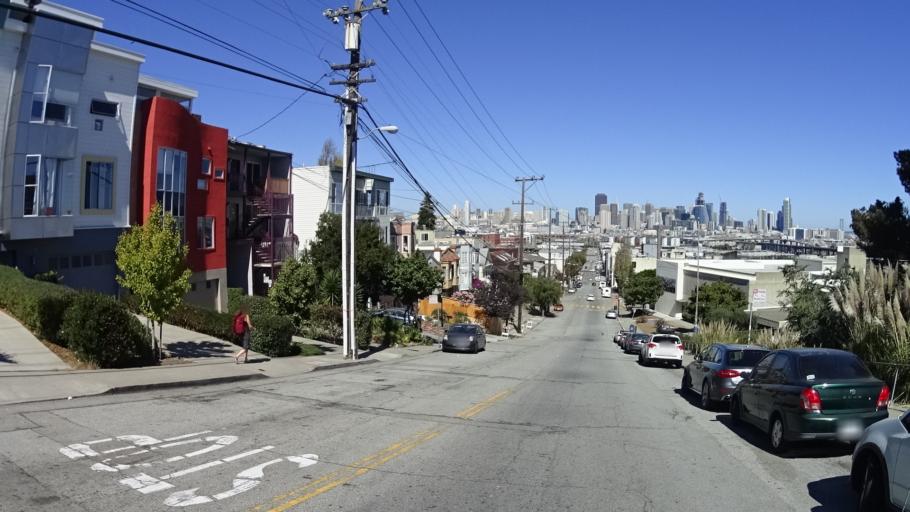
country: US
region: California
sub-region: San Francisco County
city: San Francisco
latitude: 37.7611
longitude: -122.4012
